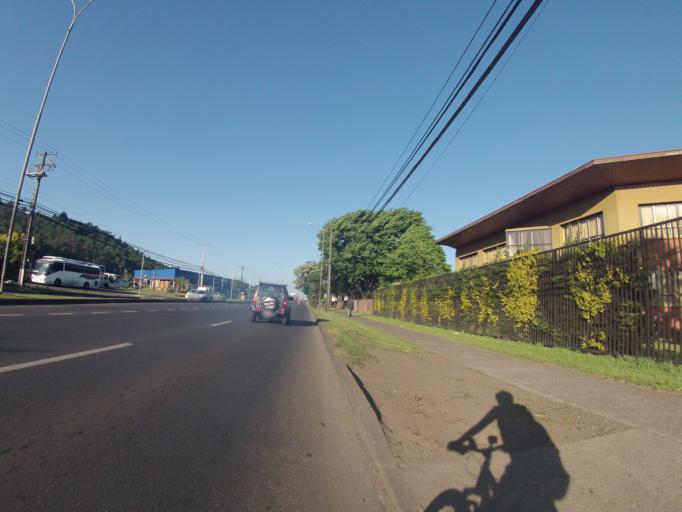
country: CL
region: Araucania
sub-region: Provincia de Cautin
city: Temuco
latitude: -38.7315
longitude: -72.5851
